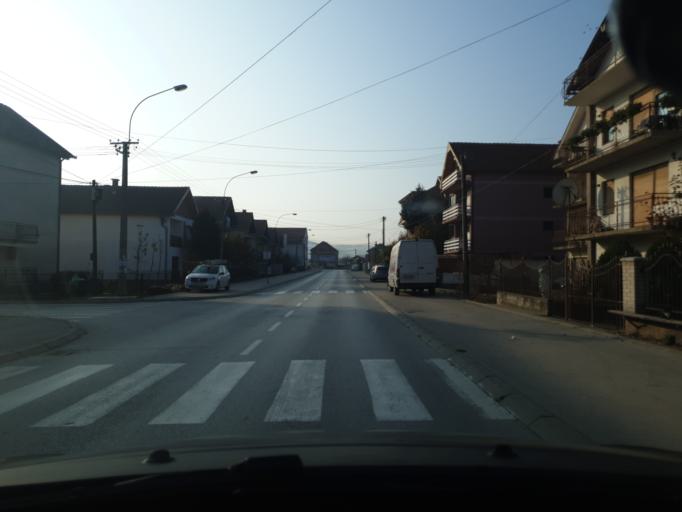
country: RS
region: Central Serbia
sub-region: Jablanicki Okrug
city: Leskovac
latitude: 42.9983
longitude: 21.9236
